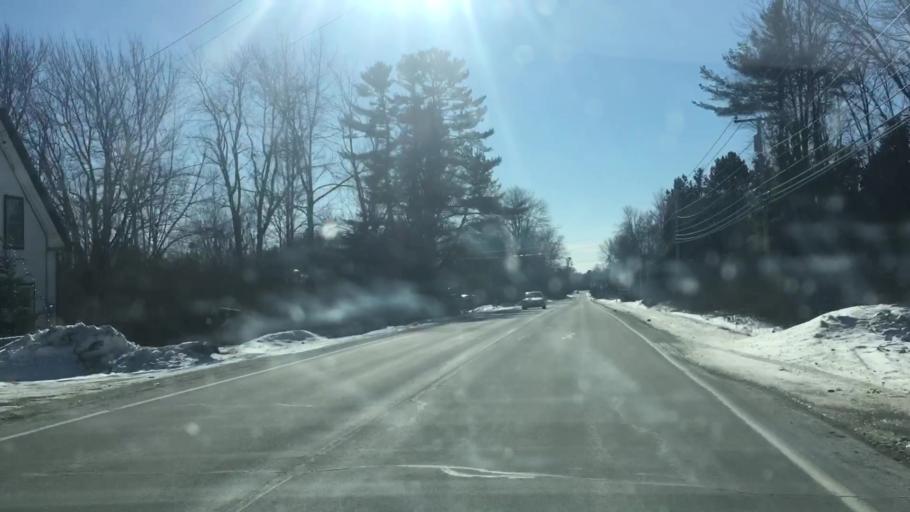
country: US
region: Maine
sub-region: Hancock County
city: Ellsworth
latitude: 44.5051
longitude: -68.4403
